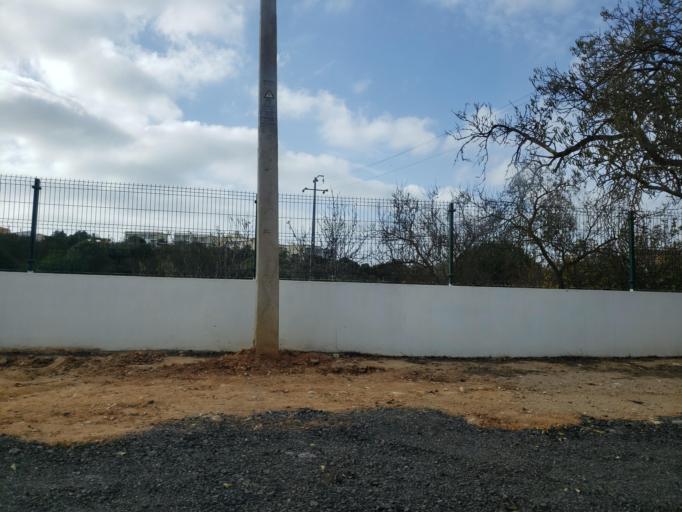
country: PT
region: Faro
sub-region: Portimao
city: Portimao
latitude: 37.1528
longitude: -8.5593
